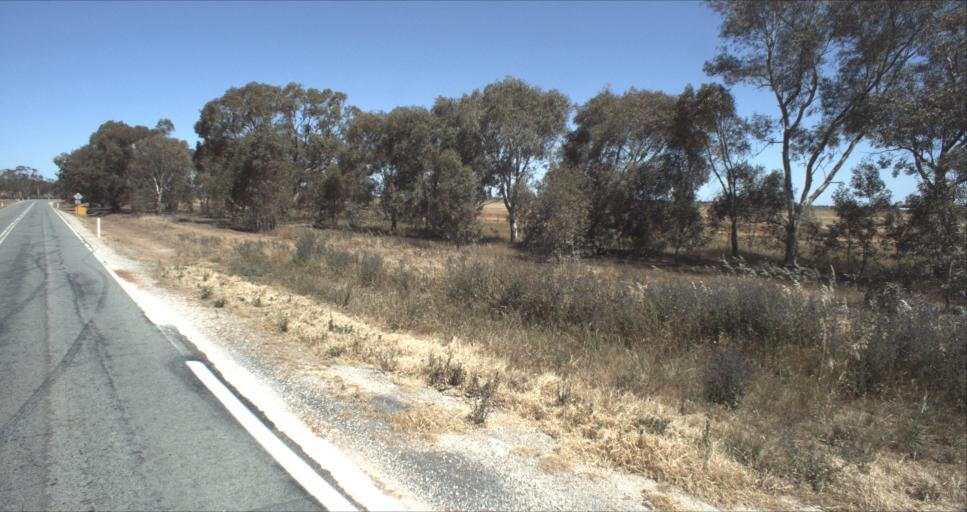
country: AU
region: New South Wales
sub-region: Leeton
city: Leeton
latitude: -34.4943
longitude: 146.4324
